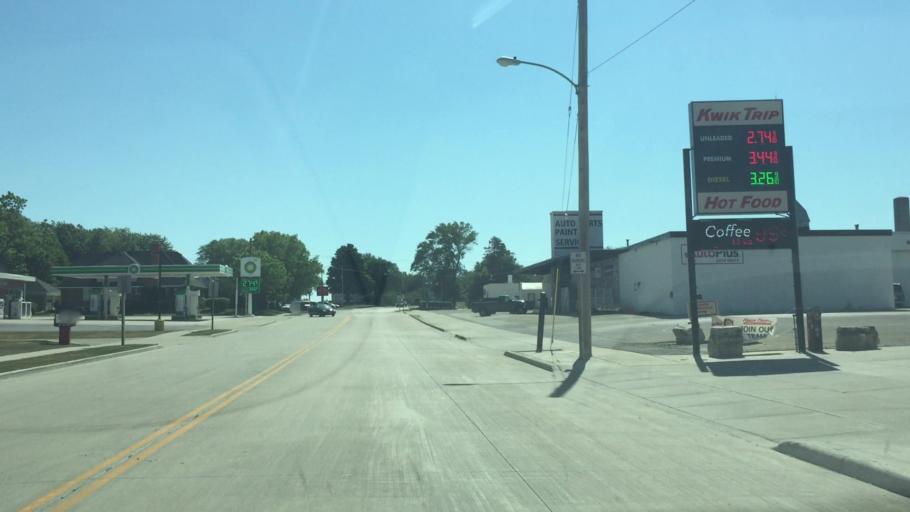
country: US
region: Wisconsin
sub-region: Calumet County
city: Chilton
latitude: 44.0241
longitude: -88.1610
